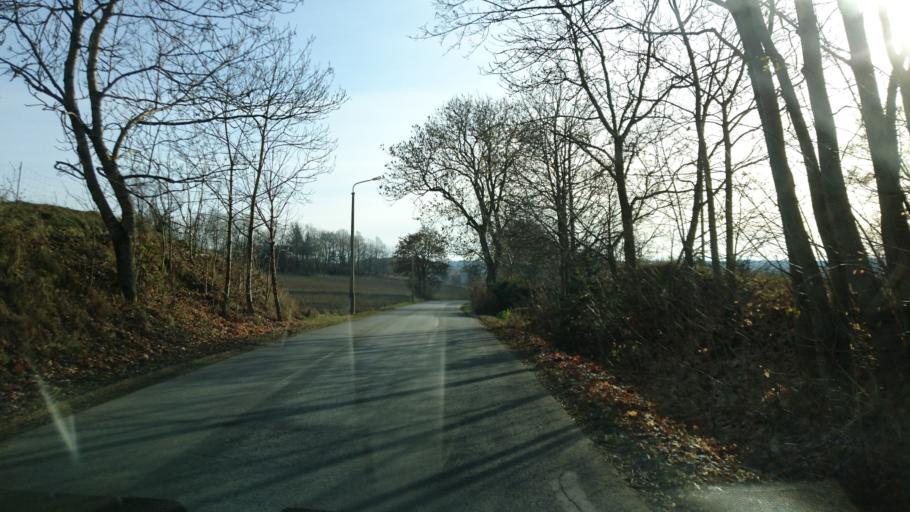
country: DE
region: Thuringia
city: Tanna
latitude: 50.5017
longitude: 11.8632
